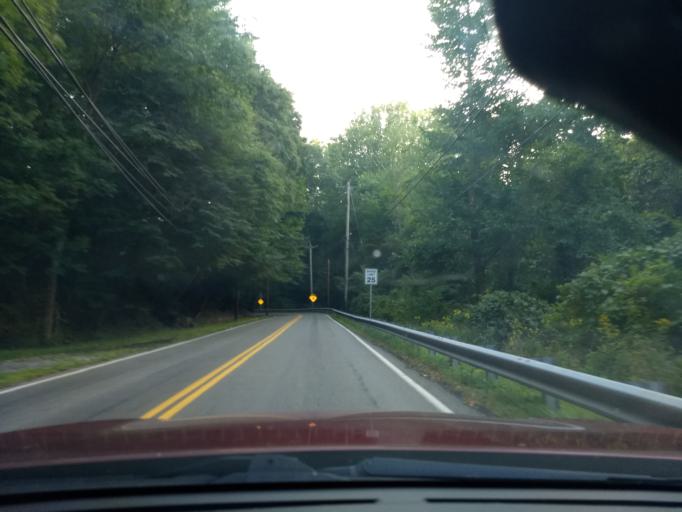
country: US
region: Pennsylvania
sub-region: Allegheny County
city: Coraopolis
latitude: 40.5522
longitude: -80.1492
